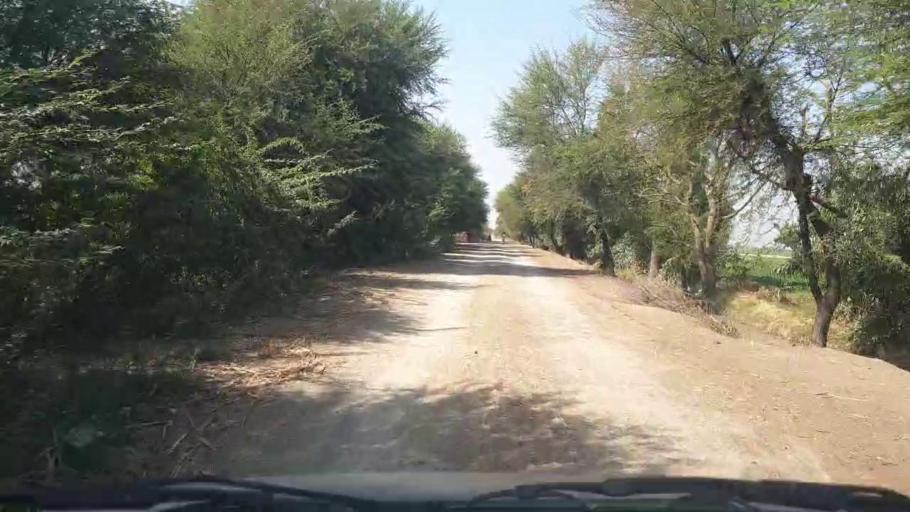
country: PK
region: Sindh
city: Samaro
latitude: 25.2372
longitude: 69.3279
